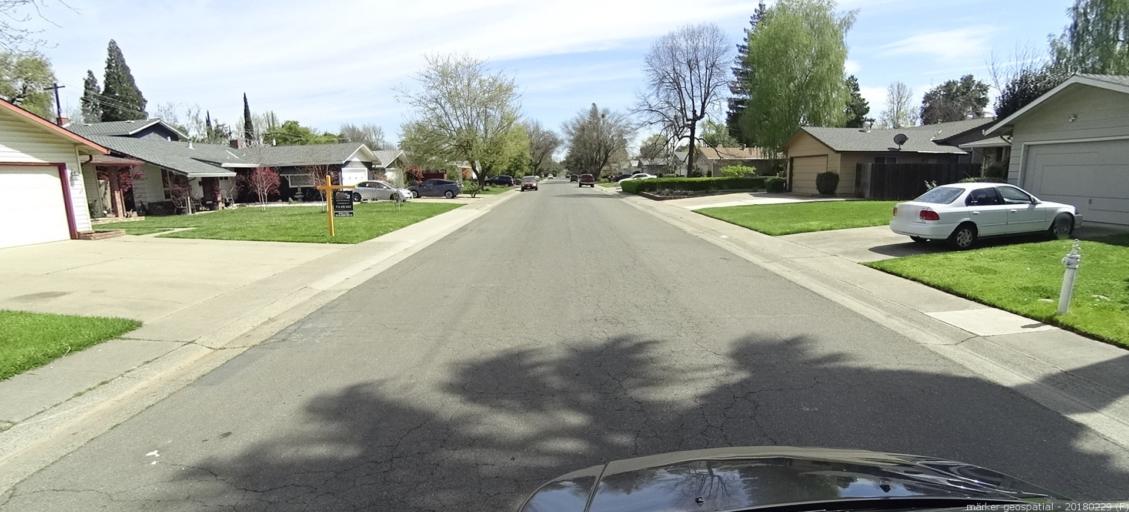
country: US
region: California
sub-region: Sacramento County
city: Rosemont
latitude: 38.5538
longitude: -121.3702
